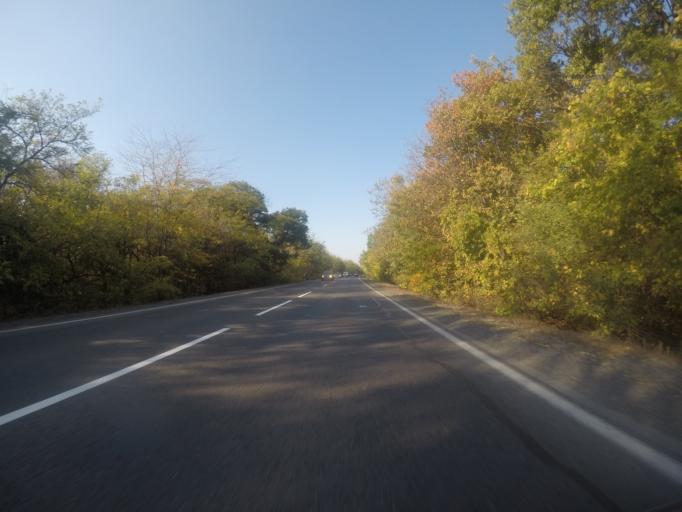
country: HU
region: Fejer
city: dunaujvaros
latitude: 46.9431
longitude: 18.9165
